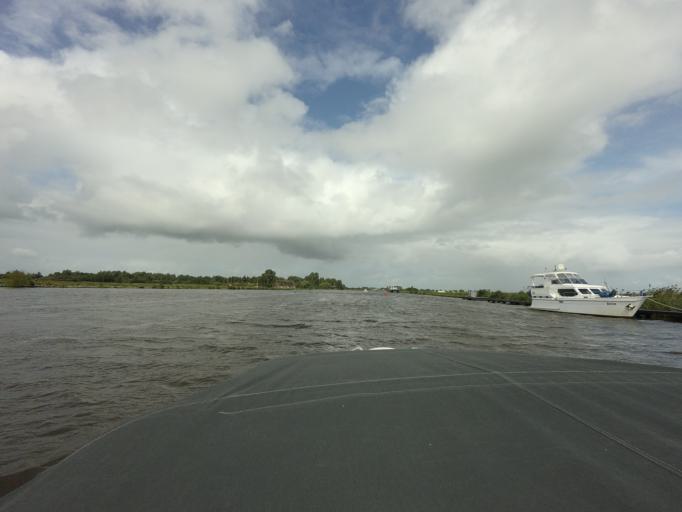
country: NL
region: Friesland
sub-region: Gemeente Boarnsterhim
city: Warten
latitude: 53.1360
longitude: 5.9177
